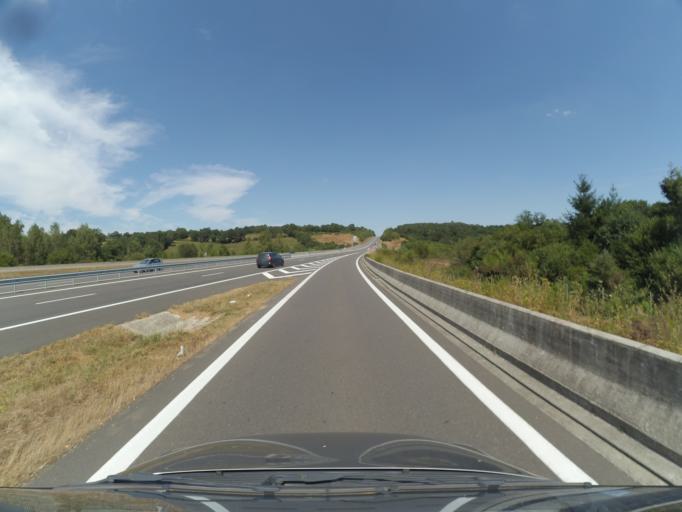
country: FR
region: Poitou-Charentes
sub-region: Departement de la Charente
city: Etagnac
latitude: 45.8909
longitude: 0.8180
